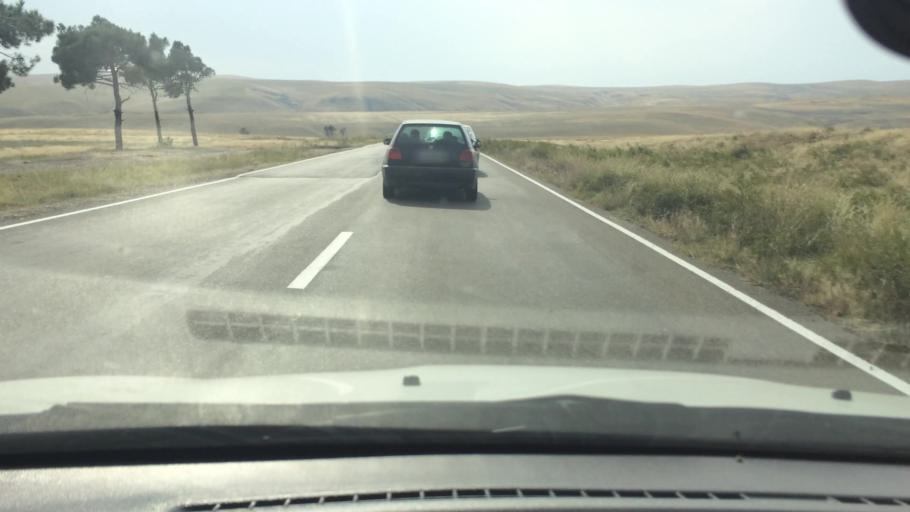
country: GE
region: Kvemo Kartli
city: Rust'avi
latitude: 41.5309
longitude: 44.9412
